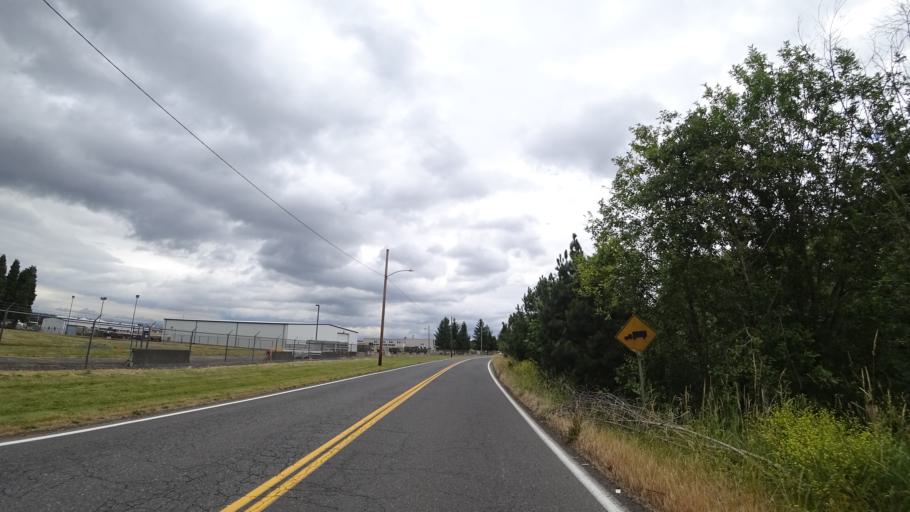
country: US
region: Washington
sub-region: Clark County
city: Vancouver
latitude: 45.5756
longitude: -122.6017
